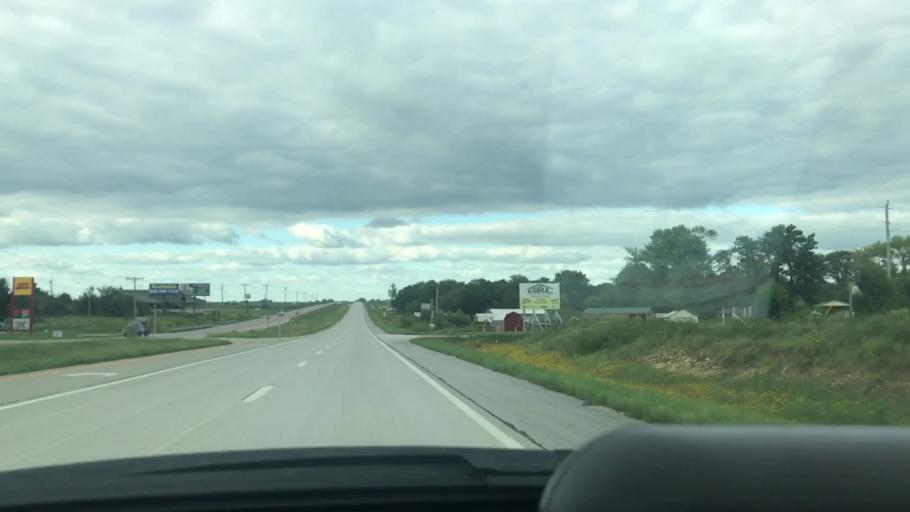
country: US
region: Missouri
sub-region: Benton County
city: Lincoln
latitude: 38.3470
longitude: -93.3401
